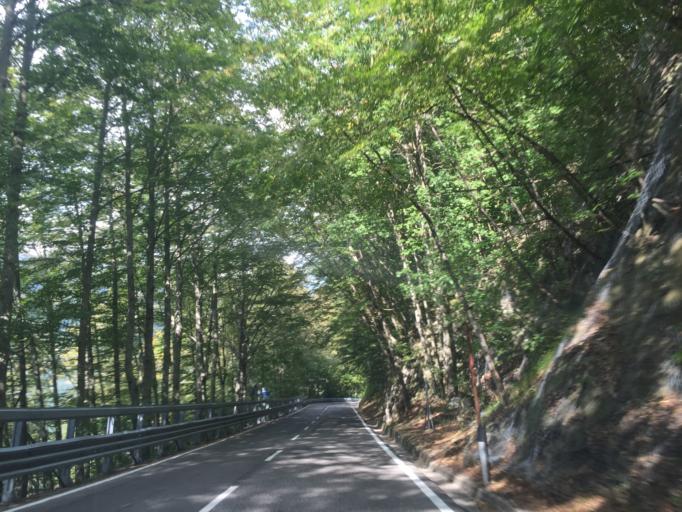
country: IT
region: Tuscany
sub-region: Provincia di Pistoia
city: Cutigliano
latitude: 44.1226
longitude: 10.7215
